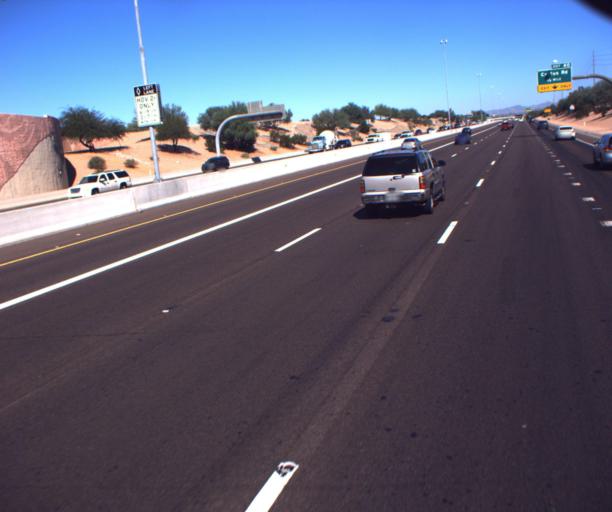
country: US
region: Arizona
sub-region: Maricopa County
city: Paradise Valley
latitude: 33.5880
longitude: -111.8914
